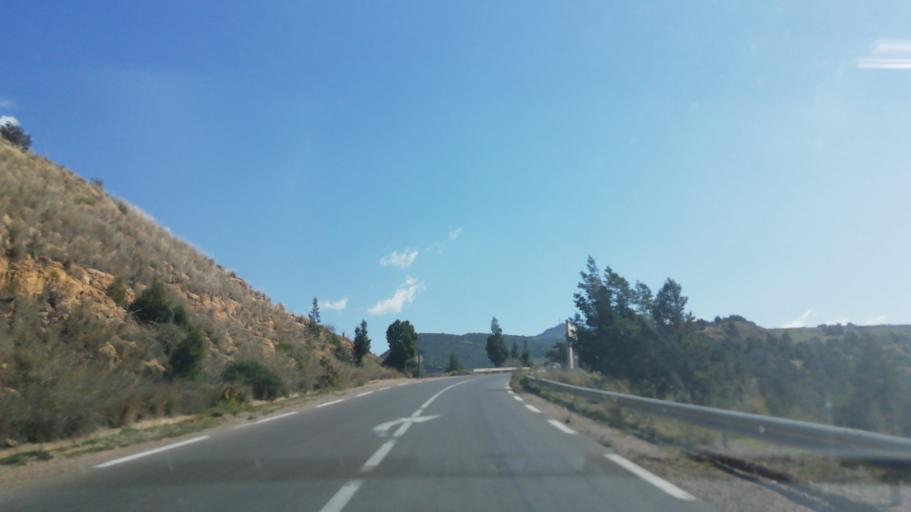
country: DZ
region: Mascara
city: Mascara
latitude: 35.4980
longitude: 0.1321
